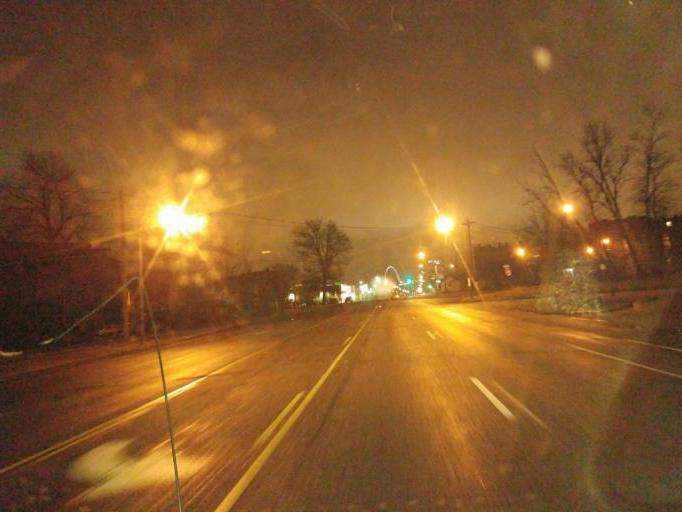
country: US
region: Missouri
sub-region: City of Saint Louis
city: St. Louis
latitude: 38.6522
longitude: -90.2010
